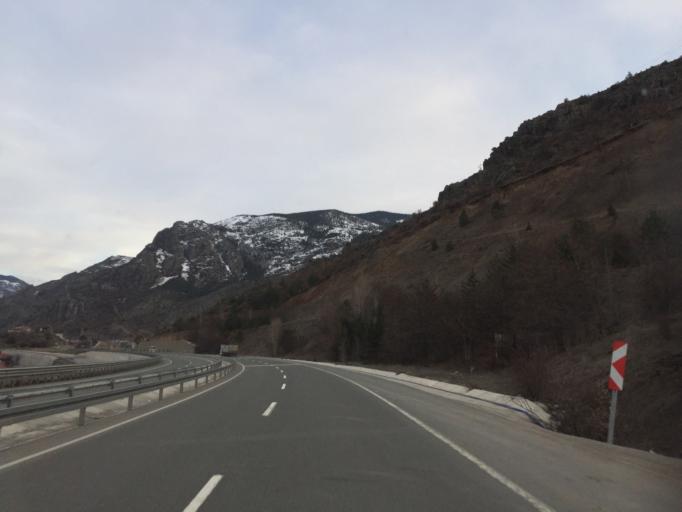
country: TR
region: Gumushane
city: Gumushkhane
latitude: 40.5057
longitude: 39.4234
